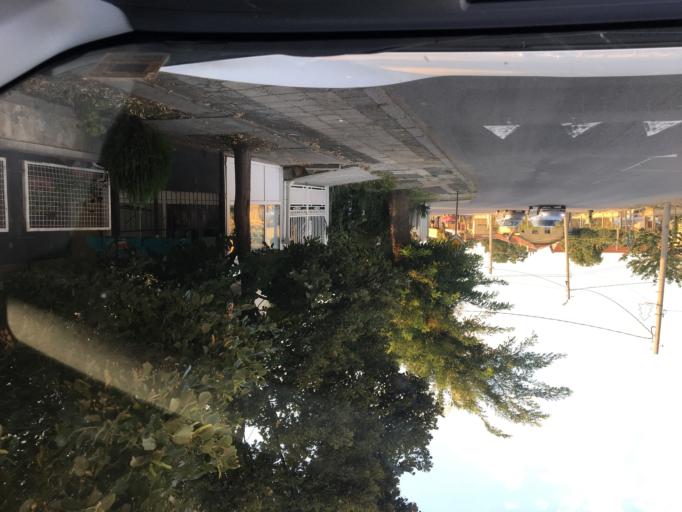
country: BG
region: Burgas
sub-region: Obshtina Burgas
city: Burgas
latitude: 42.6120
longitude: 27.4931
